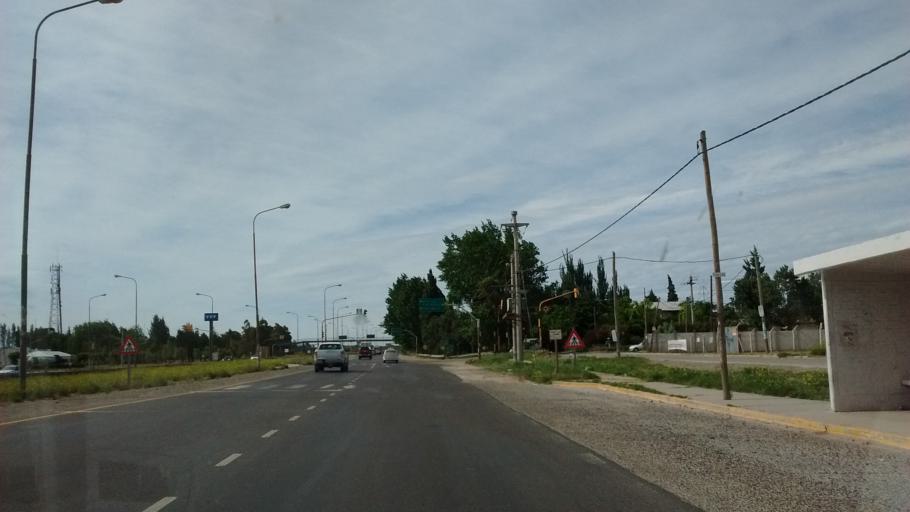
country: AR
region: Neuquen
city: Neuquen
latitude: -38.9078
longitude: -68.0829
